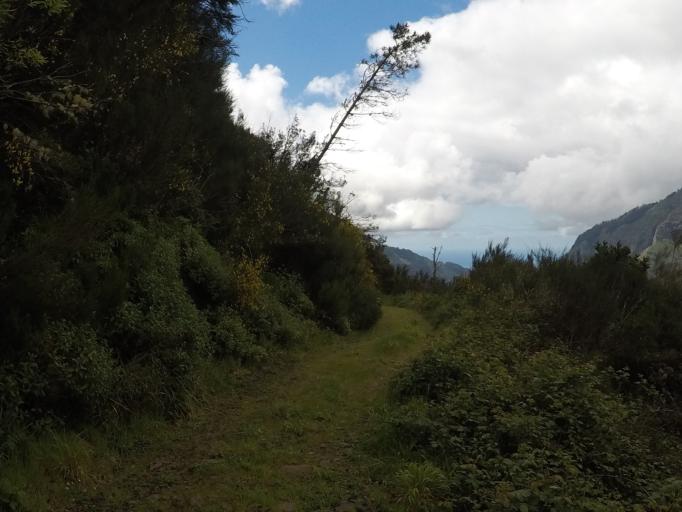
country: PT
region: Madeira
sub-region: Sao Vicente
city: Sao Vicente
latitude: 32.7505
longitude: -17.0179
